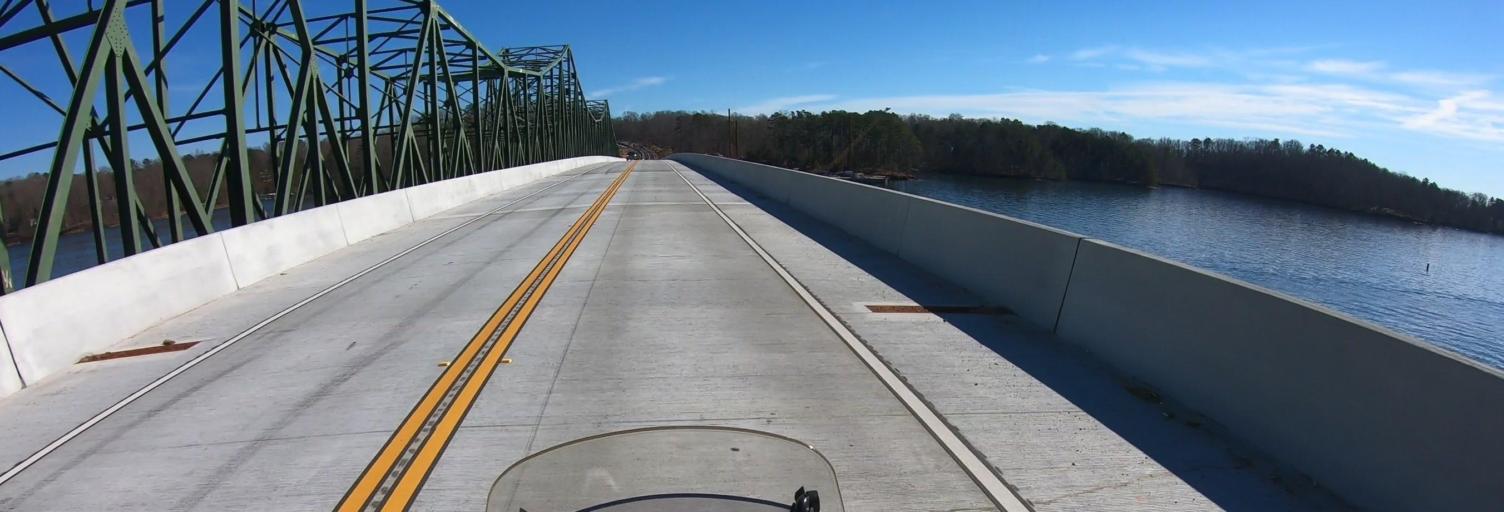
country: US
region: Georgia
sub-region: Hall County
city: Oakwood
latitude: 34.2620
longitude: -83.9522
